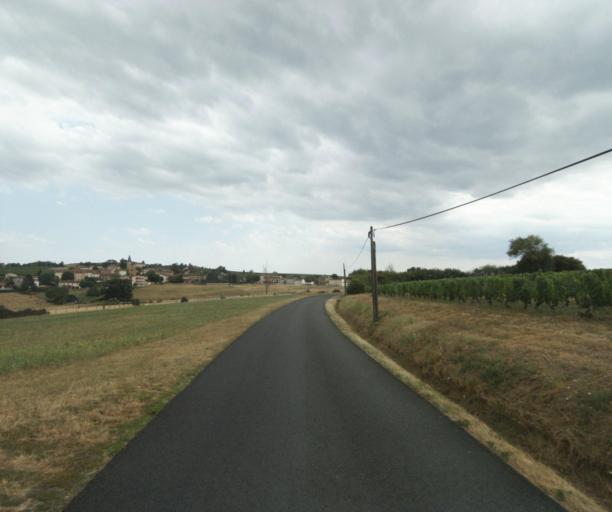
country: FR
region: Rhone-Alpes
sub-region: Departement du Rhone
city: Saint-Romain-de-Popey
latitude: 45.8831
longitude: 4.5532
